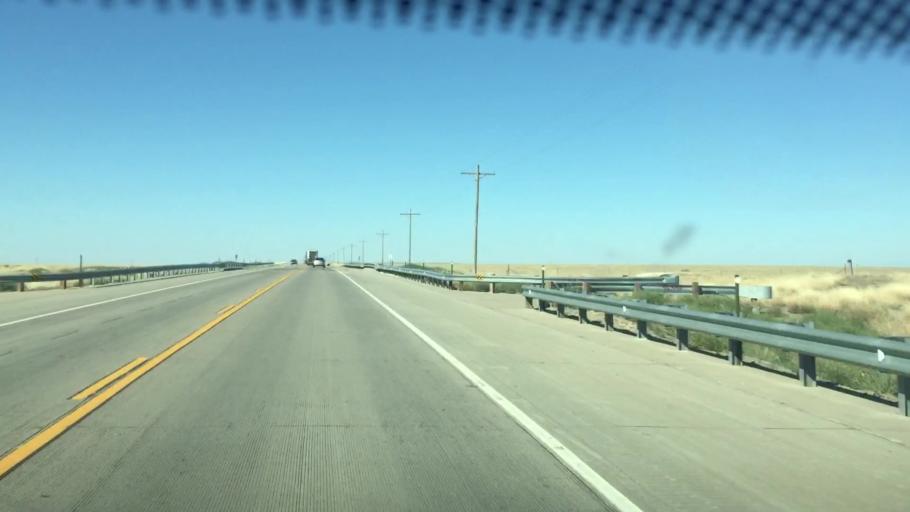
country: US
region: Colorado
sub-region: Prowers County
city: Lamar
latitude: 38.2374
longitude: -102.7239
